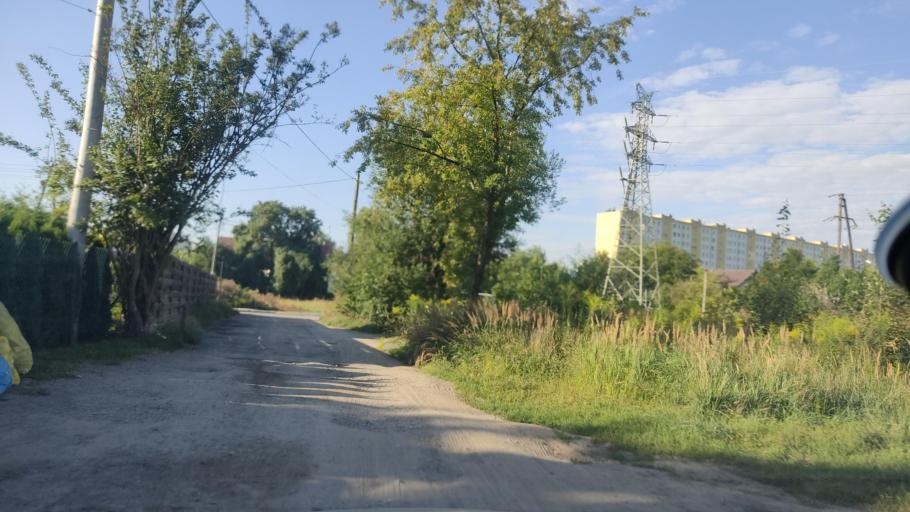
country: PL
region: Lesser Poland Voivodeship
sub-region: Powiat krakowski
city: Zielonki
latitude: 50.0962
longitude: 19.9286
